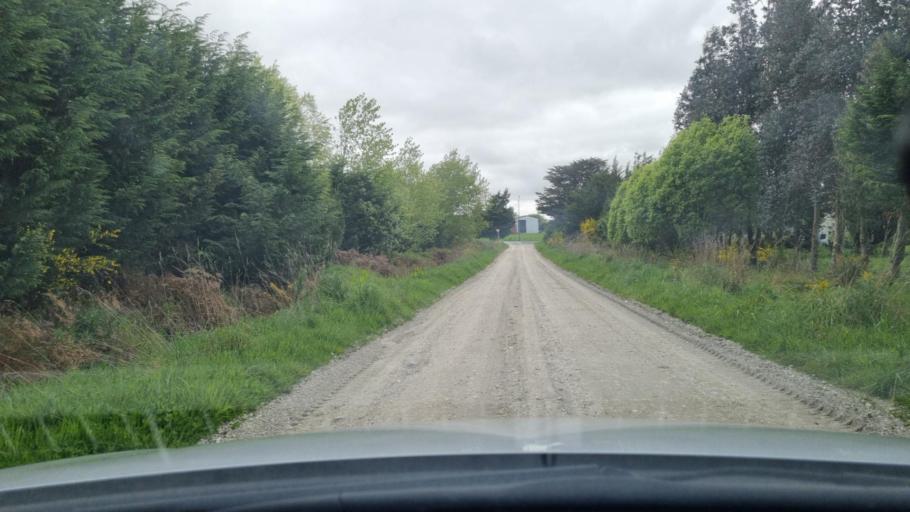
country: NZ
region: Southland
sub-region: Invercargill City
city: Invercargill
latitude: -46.4337
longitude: 168.3896
